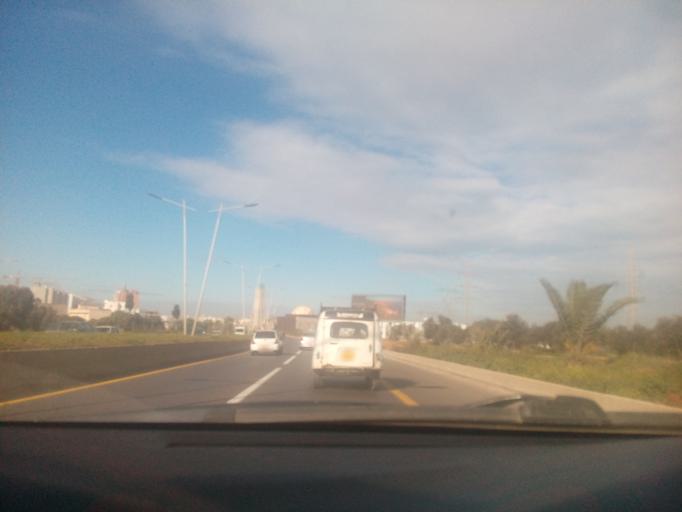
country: DZ
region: Oran
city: Es Senia
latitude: 35.6750
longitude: -0.5974
